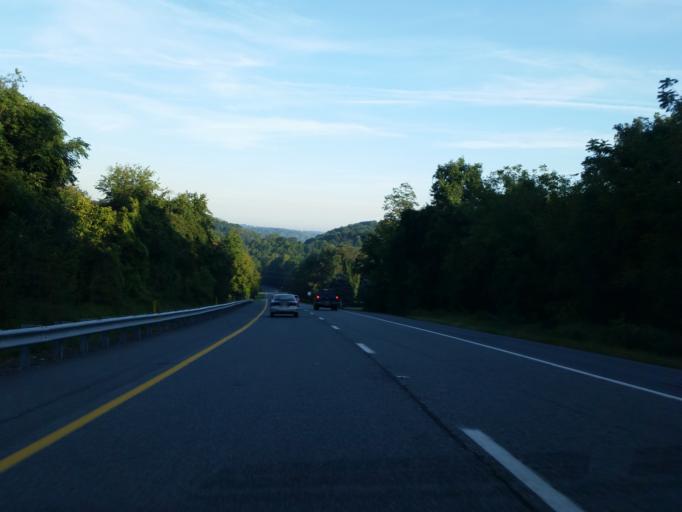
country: US
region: Pennsylvania
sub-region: Lancaster County
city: Willow Street
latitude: 39.9190
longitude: -76.2464
